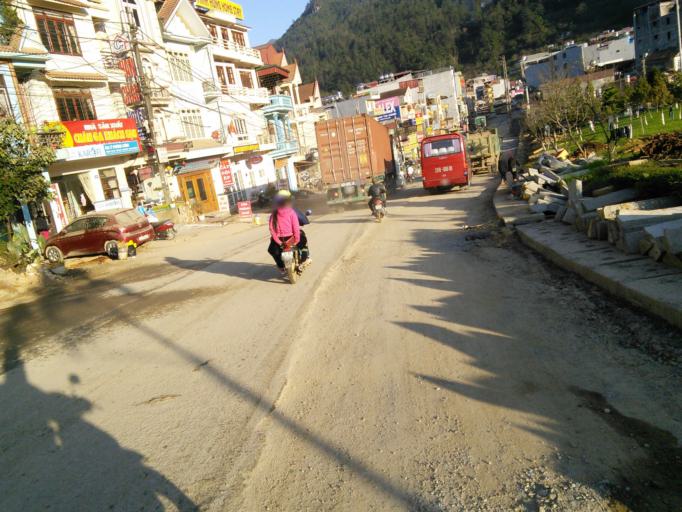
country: VN
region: Lao Cai
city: Sa Pa
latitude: 22.3397
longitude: 103.8492
